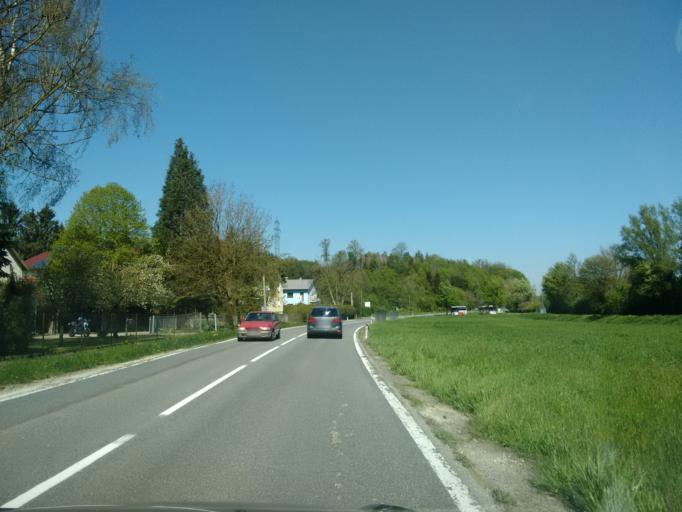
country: AT
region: Upper Austria
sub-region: Politischer Bezirk Steyr-Land
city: Bad Hall
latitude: 48.0474
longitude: 14.2056
